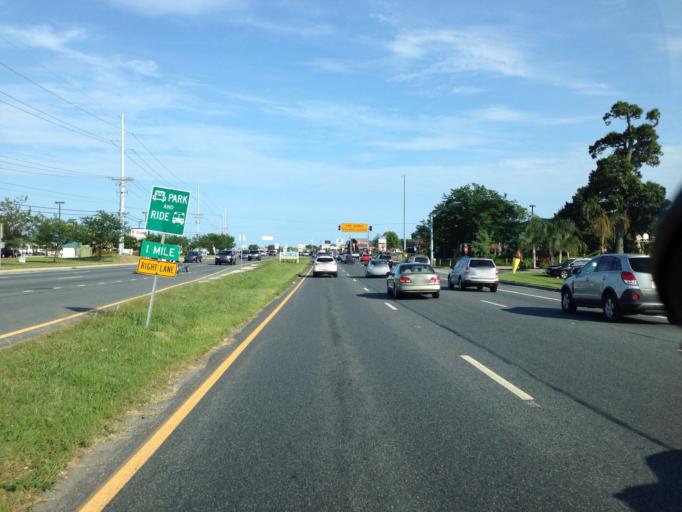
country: US
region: Delaware
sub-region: Sussex County
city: Rehoboth Beach
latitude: 38.7232
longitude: -75.1230
